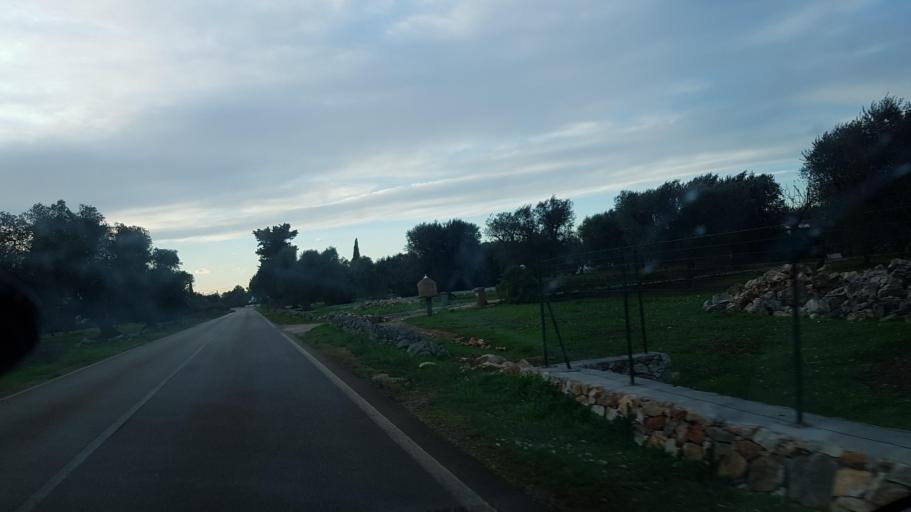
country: IT
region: Apulia
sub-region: Provincia di Brindisi
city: San Vito dei Normanni
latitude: 40.6478
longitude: 17.6736
